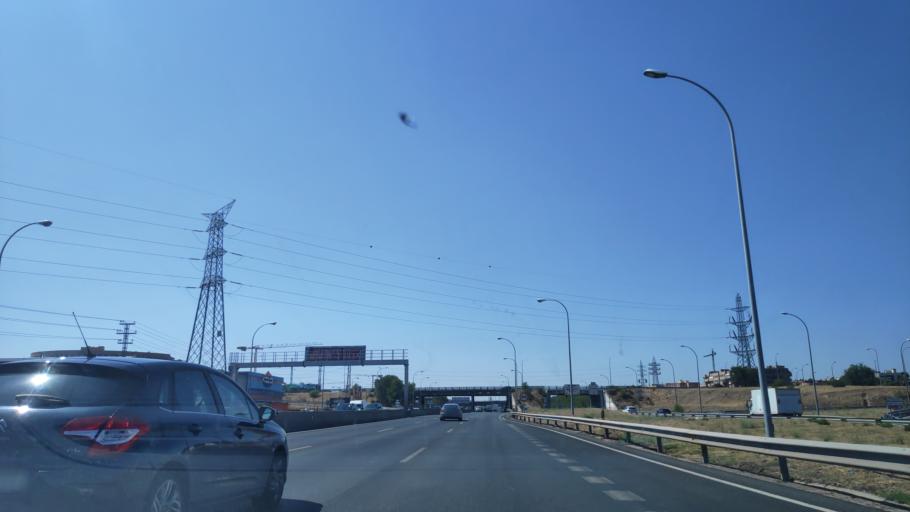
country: ES
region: Madrid
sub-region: Provincia de Madrid
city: Getafe
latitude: 40.3244
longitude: -3.7291
